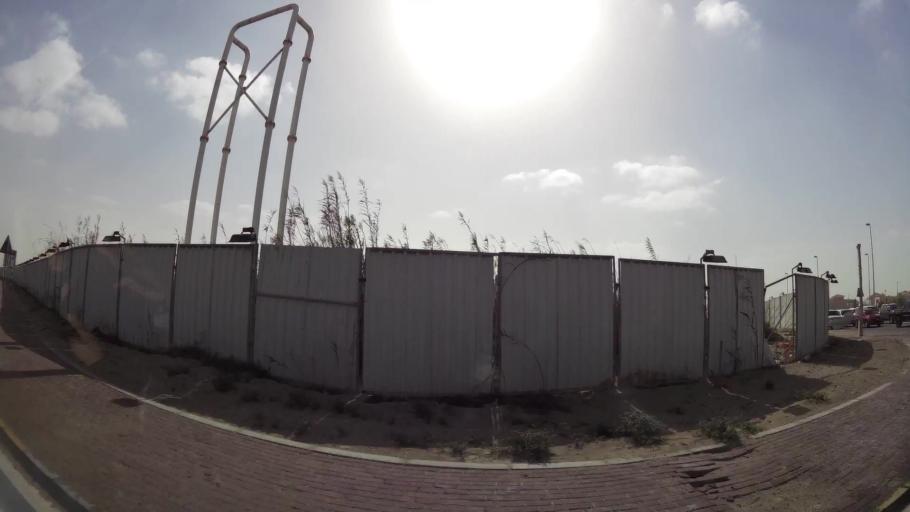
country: AE
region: Abu Dhabi
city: Abu Dhabi
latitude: 24.4294
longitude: 54.5633
